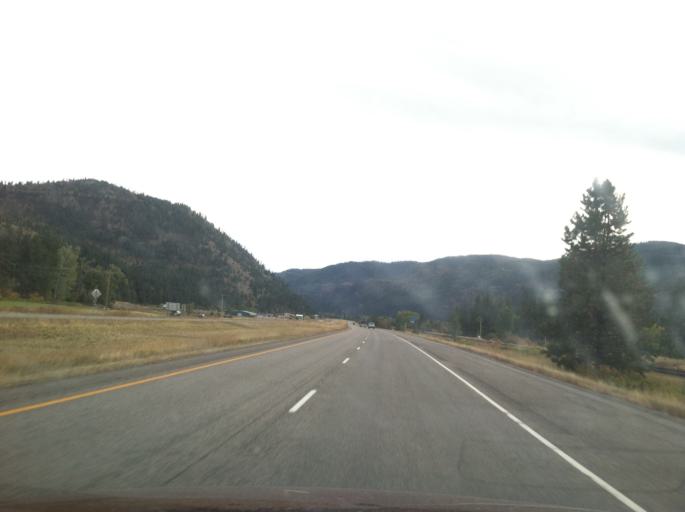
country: US
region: Montana
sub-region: Missoula County
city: Clinton
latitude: 46.7681
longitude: -113.7112
